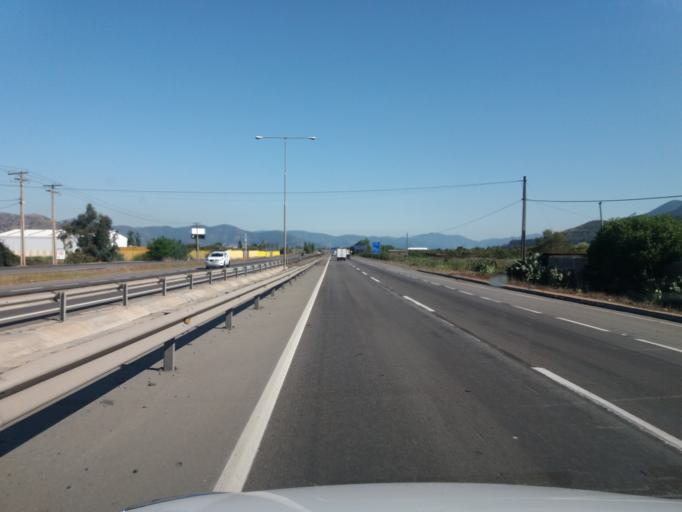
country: CL
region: Valparaiso
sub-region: Provincia de Quillota
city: Hacienda La Calera
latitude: -32.8132
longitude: -71.1454
